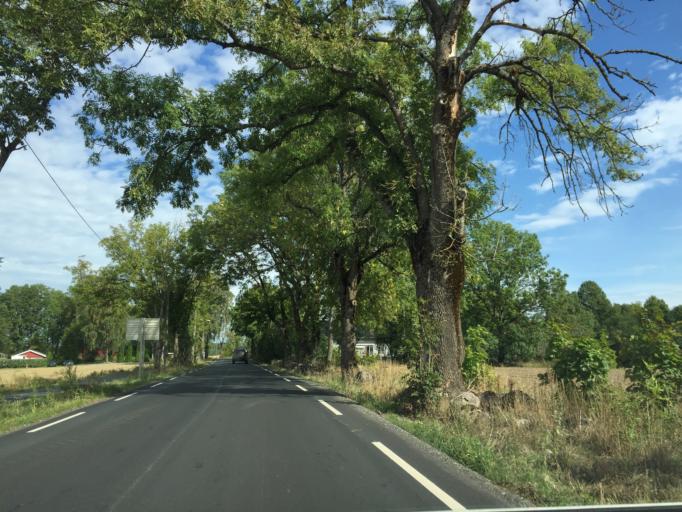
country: NO
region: Akershus
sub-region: As
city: As
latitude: 59.7084
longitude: 10.7718
